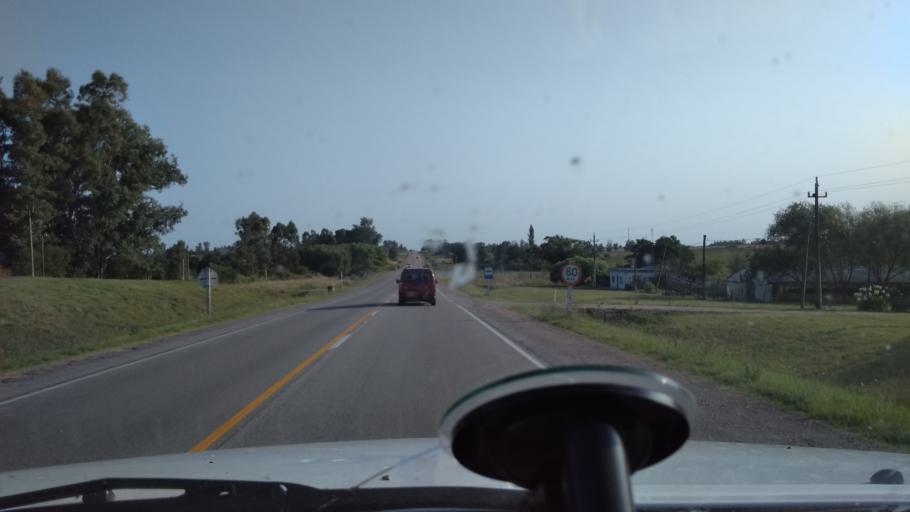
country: UY
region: Canelones
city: Sauce
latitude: -34.6132
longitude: -56.0489
